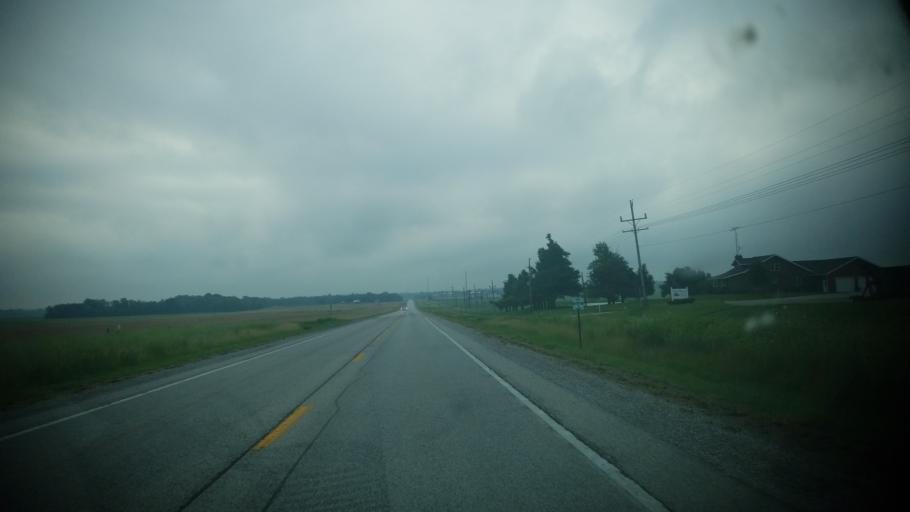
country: US
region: Illinois
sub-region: Clay County
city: Flora
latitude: 38.6775
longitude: -88.3878
